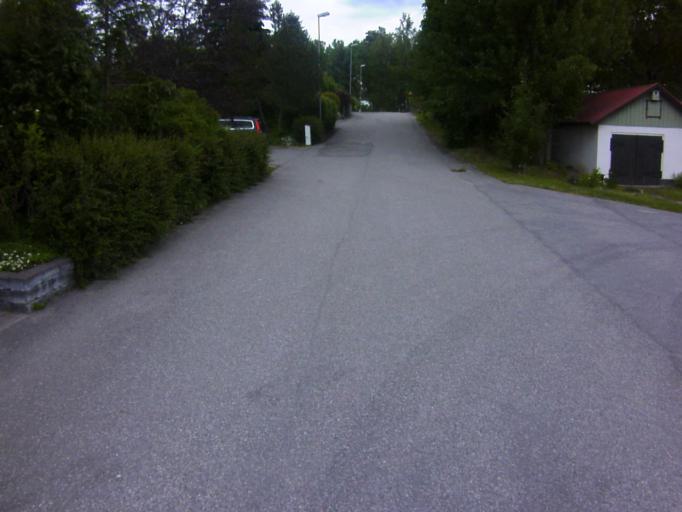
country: SE
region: Soedermanland
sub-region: Eskilstuna Kommun
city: Skogstorp
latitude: 59.3207
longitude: 16.4734
